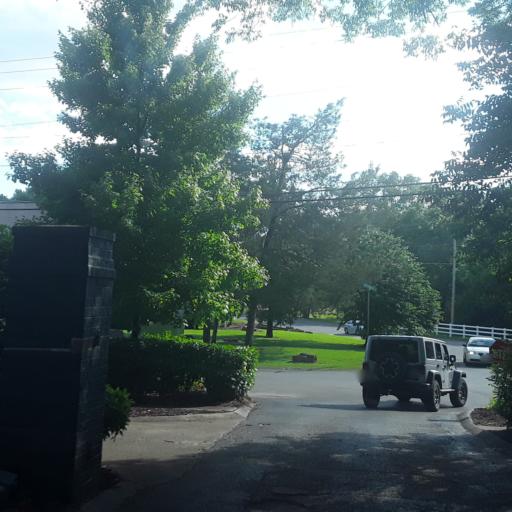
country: US
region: Tennessee
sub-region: Wilson County
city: Green Hill
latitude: 36.1804
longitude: -86.6028
